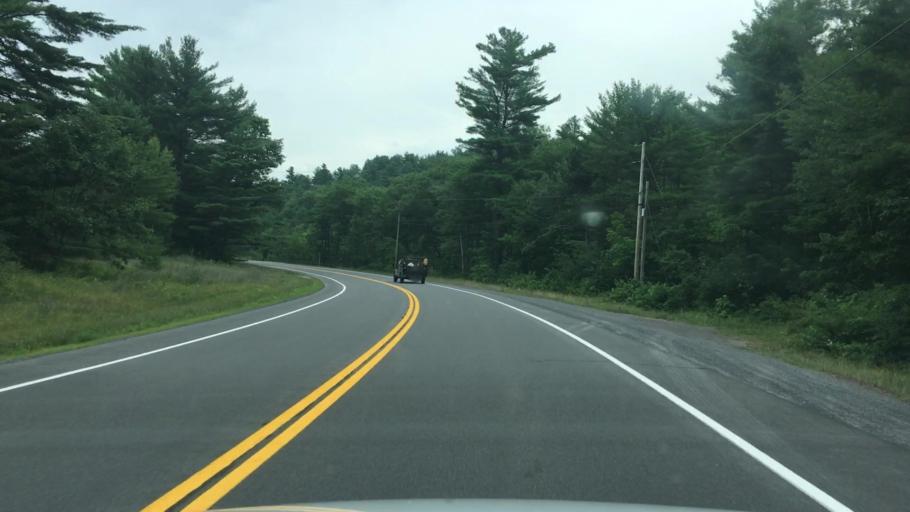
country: US
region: New York
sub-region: Essex County
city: Keeseville
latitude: 44.4552
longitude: -73.6150
